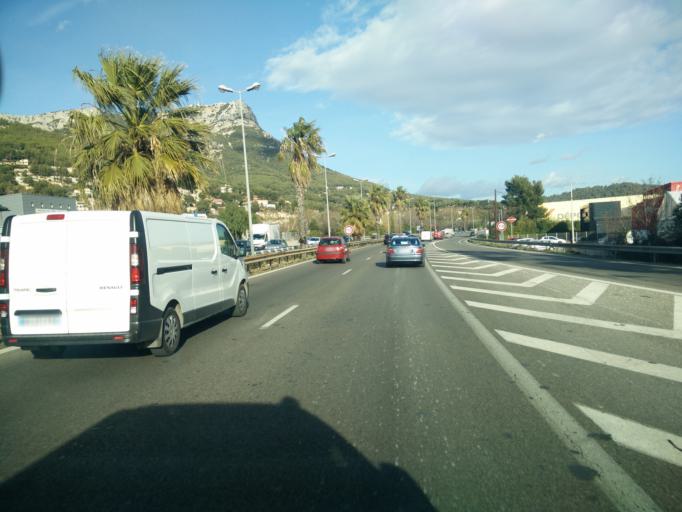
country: FR
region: Provence-Alpes-Cote d'Azur
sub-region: Departement du Var
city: La Valette-du-Var
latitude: 43.1386
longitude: 5.9967
